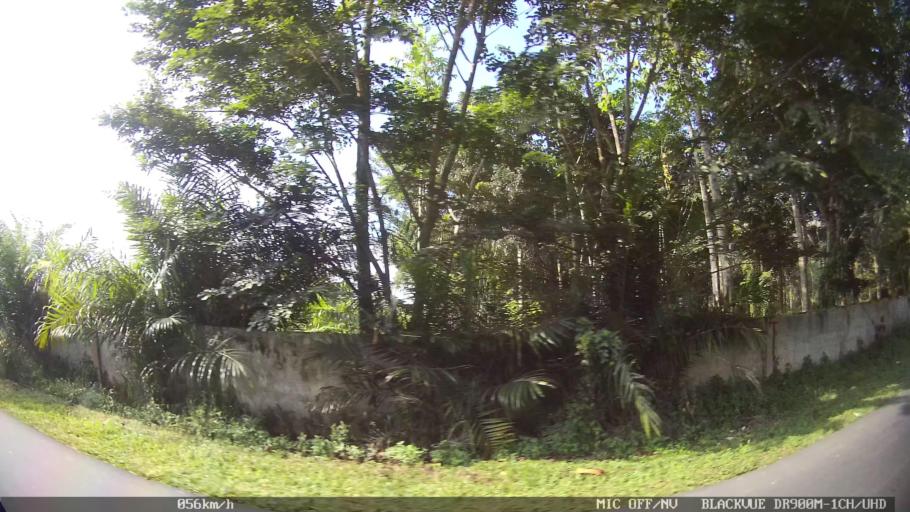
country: ID
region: North Sumatra
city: Percut
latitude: 3.5933
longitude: 98.8004
